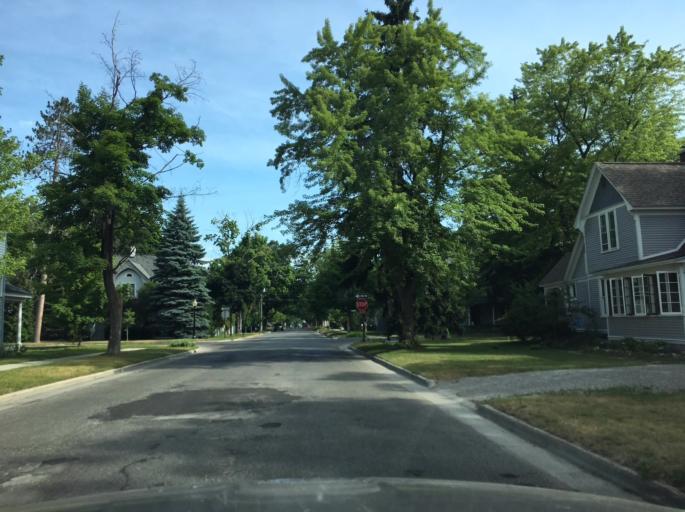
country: US
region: Michigan
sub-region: Grand Traverse County
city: Traverse City
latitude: 44.7601
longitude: -85.6329
